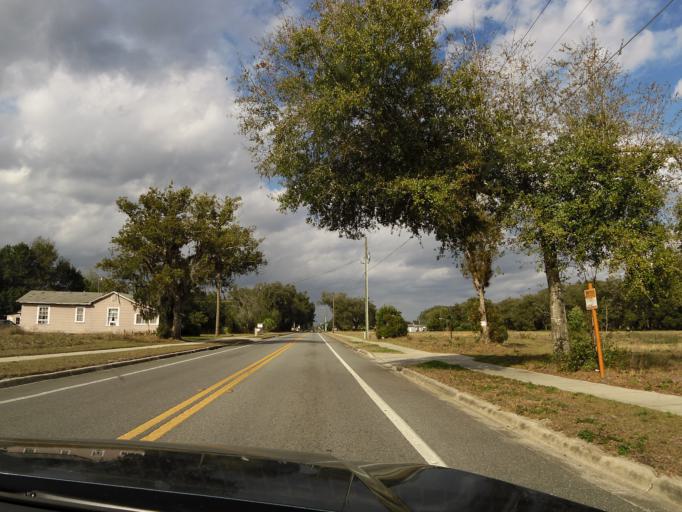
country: US
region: Florida
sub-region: Volusia County
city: Pierson
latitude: 29.2371
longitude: -81.4628
